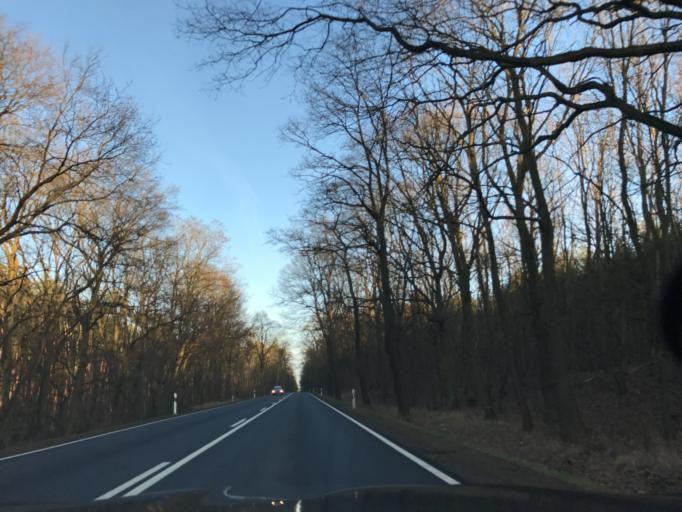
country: DE
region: Saxony-Anhalt
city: Burg bei Magdeburg
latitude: 52.2900
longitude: 11.9555
